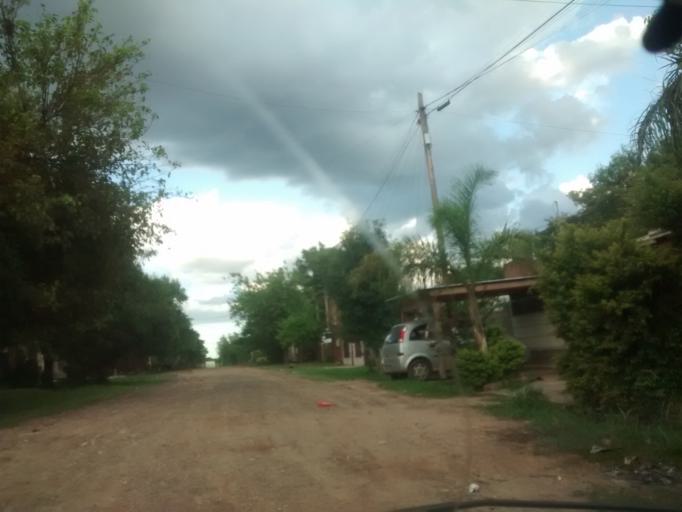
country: AR
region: Chaco
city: Fontana
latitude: -27.4283
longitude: -58.9961
